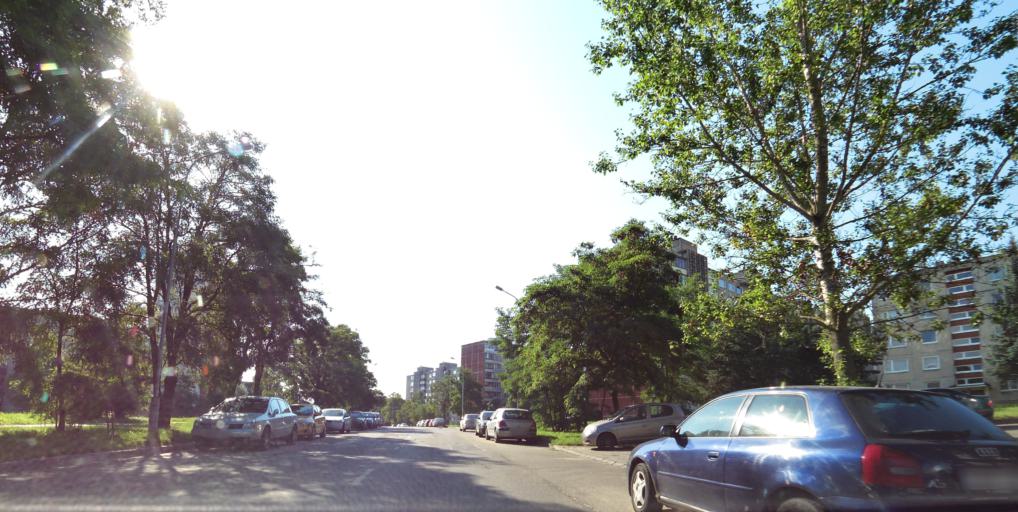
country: LT
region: Vilnius County
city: Justiniskes
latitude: 54.6966
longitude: 25.2125
